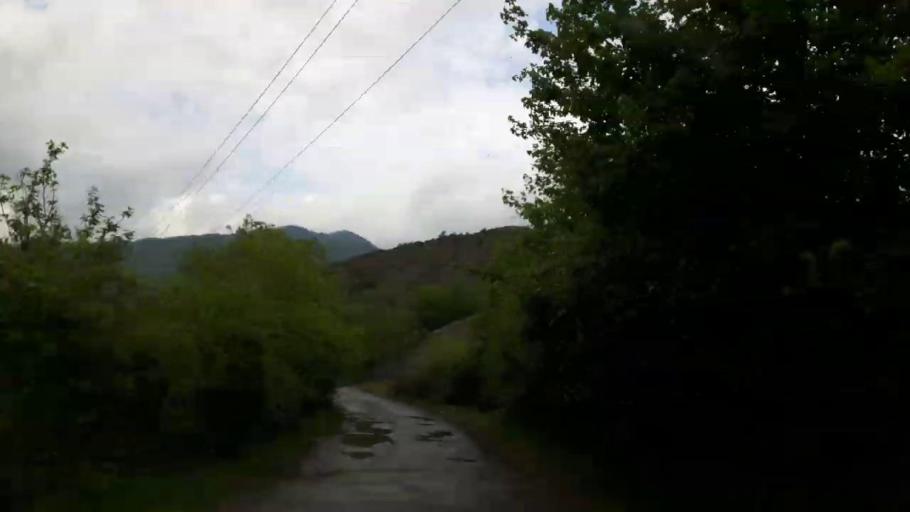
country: GE
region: Shida Kartli
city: Gori
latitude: 41.8933
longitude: 44.0206
